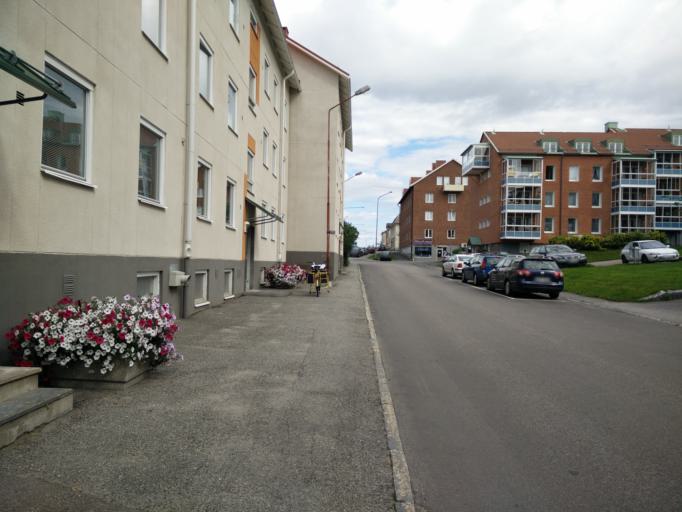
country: SE
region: Vaesternorrland
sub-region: Haernoesands Kommun
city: Haernoesand
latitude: 62.6351
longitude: 17.9428
